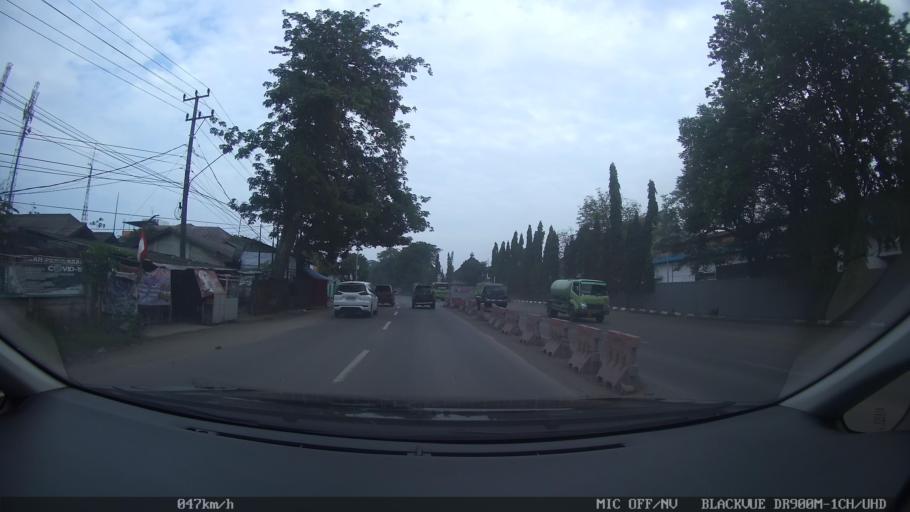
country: ID
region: Lampung
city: Panjang
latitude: -5.4558
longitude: 105.3119
